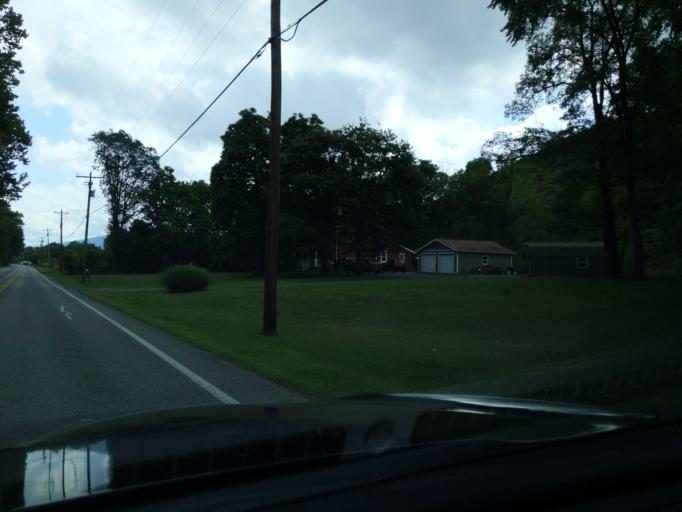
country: US
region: Pennsylvania
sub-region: Blair County
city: Duncansville
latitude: 40.3868
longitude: -78.4722
